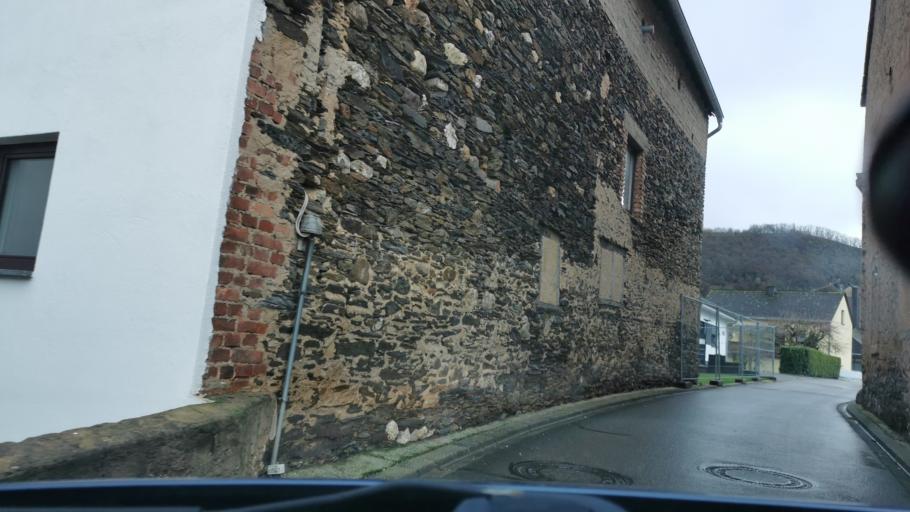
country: DE
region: Rheinland-Pfalz
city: Piesport
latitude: 49.8825
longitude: 6.9285
